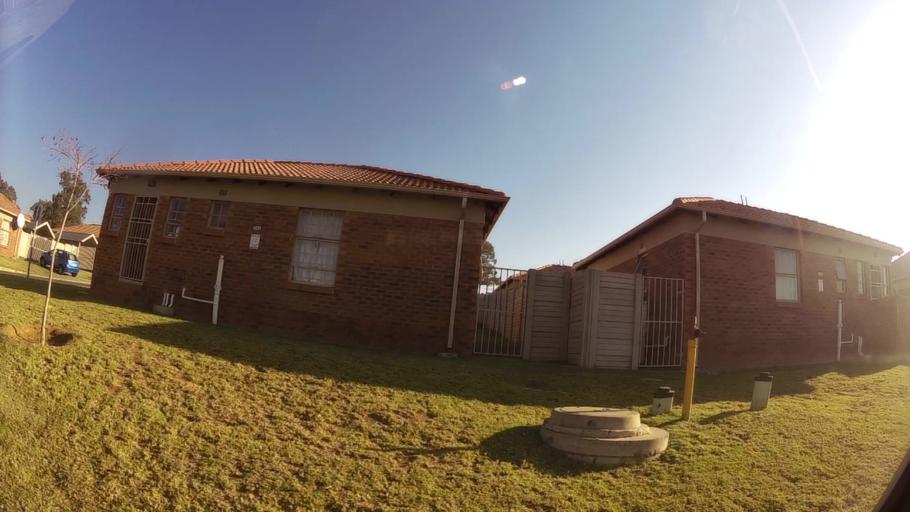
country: ZA
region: Gauteng
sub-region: City of Johannesburg Metropolitan Municipality
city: Midrand
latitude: -25.9103
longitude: 28.1075
